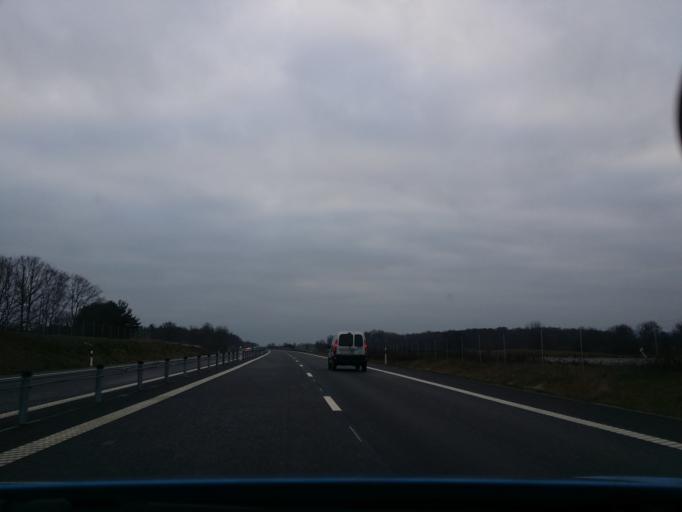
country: SE
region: Blekinge
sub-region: Karlshamns Kommun
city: Morrum
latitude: 56.1547
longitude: 14.6653
